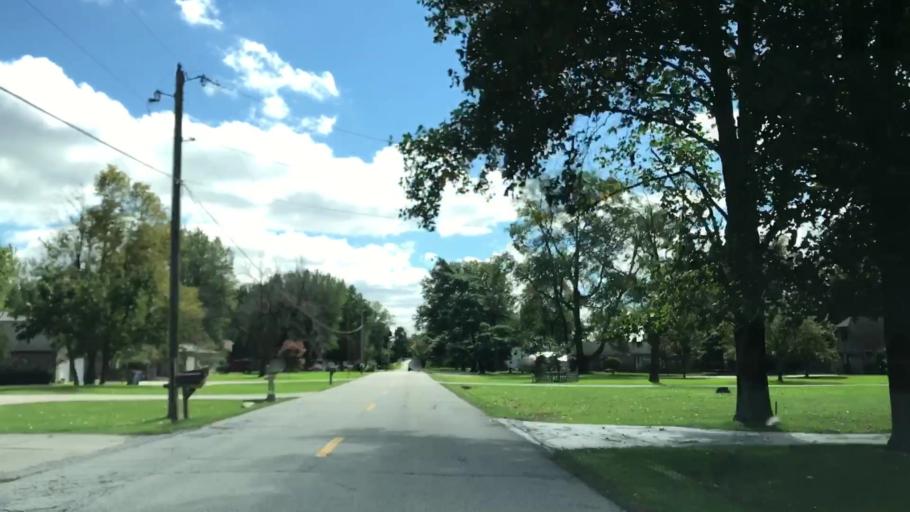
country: US
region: Indiana
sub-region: Howard County
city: Indian Heights
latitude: 40.4315
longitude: -86.1012
